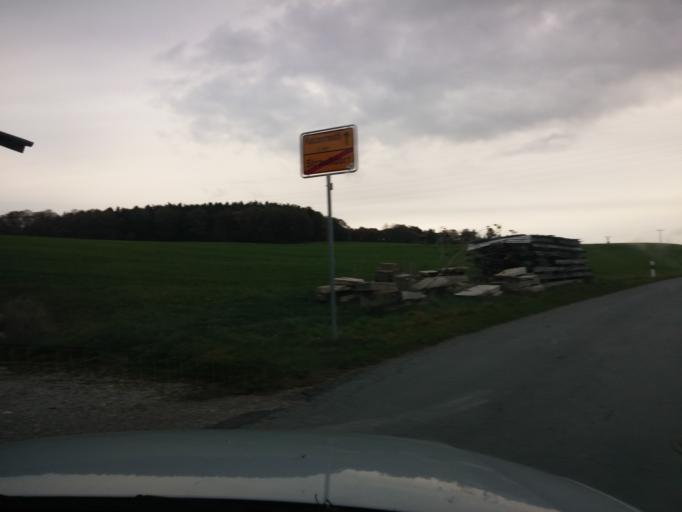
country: DE
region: Bavaria
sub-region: Upper Bavaria
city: Assling
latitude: 48.0258
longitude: 11.9960
